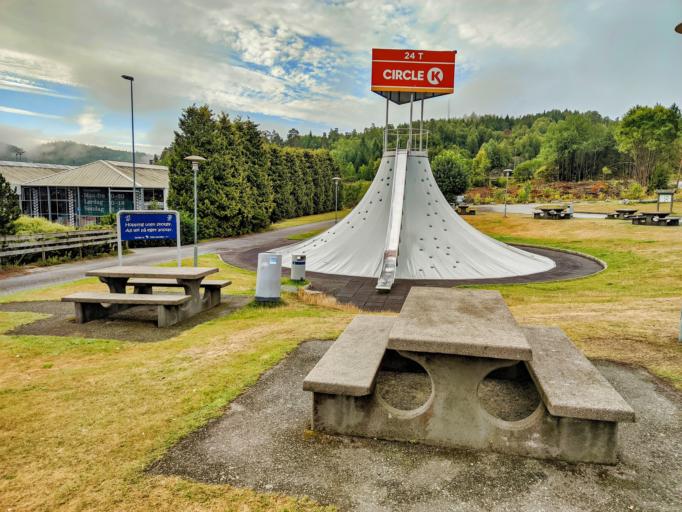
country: NO
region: Telemark
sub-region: Porsgrunn
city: Porsgrunn
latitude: 59.1212
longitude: 9.7079
